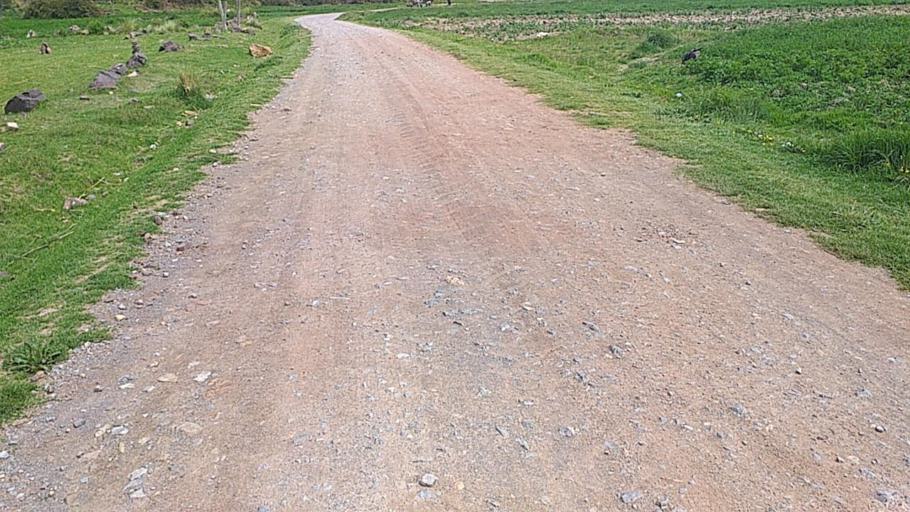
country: BO
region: La Paz
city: Batallas
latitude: -16.3465
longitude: -68.6348
